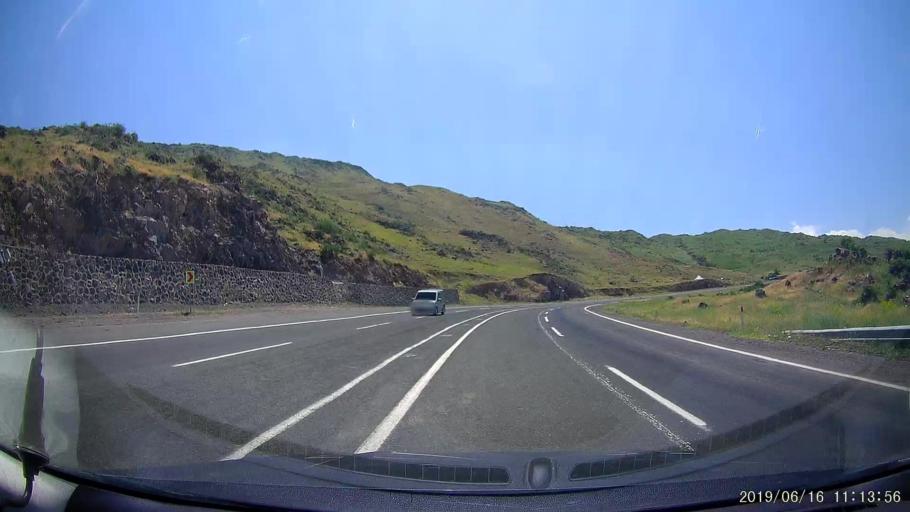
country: TR
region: Igdir
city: Igdir
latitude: 39.7859
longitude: 44.1463
